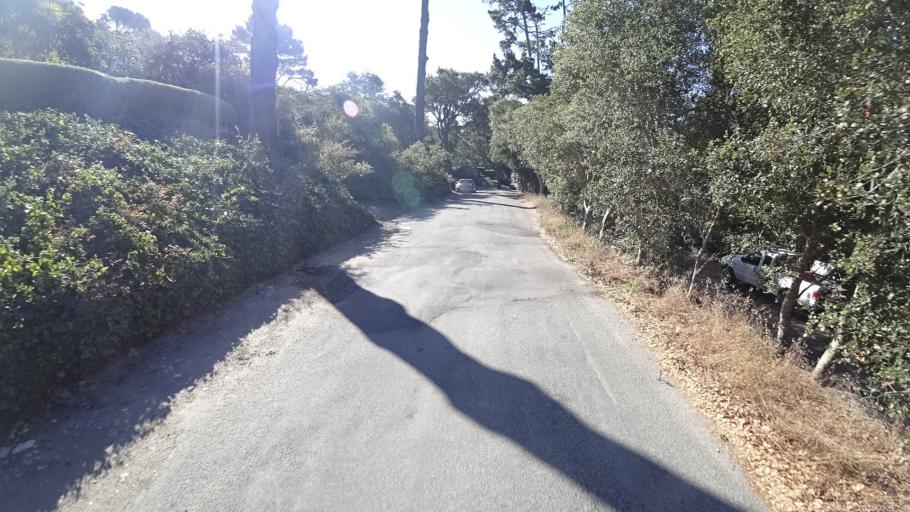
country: US
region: California
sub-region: Monterey County
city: Carmel-by-the-Sea
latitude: 36.5684
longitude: -121.9174
